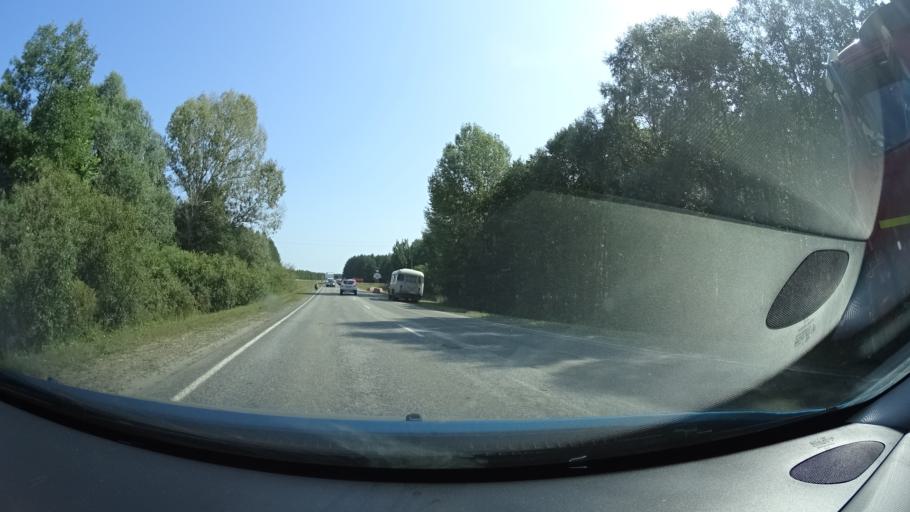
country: RU
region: Bashkortostan
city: Ulukulevo
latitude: 54.4543
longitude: 56.5120
